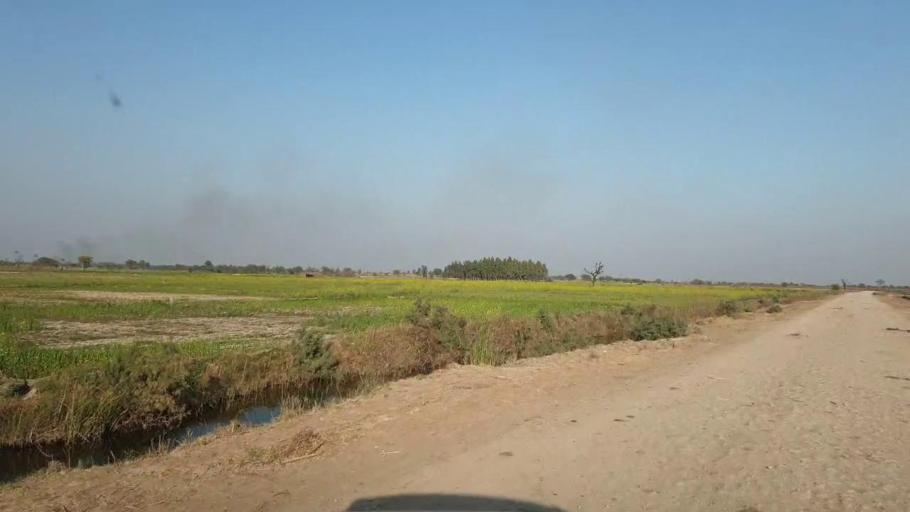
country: PK
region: Sindh
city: Chambar
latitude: 25.3408
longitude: 68.7017
